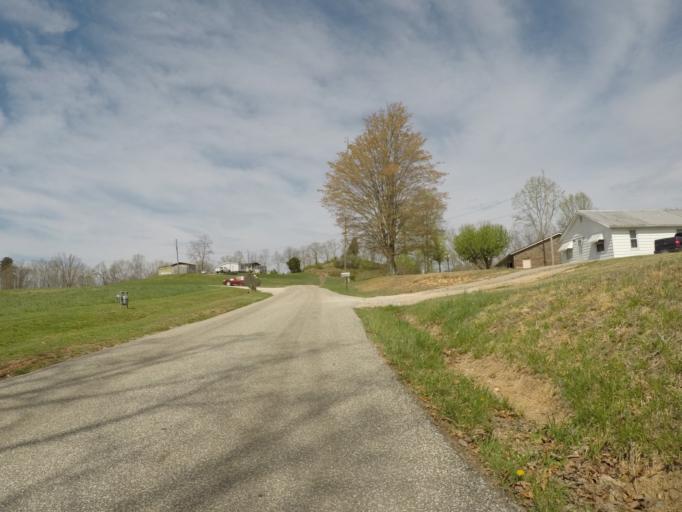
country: US
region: West Virginia
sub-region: Wayne County
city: Lavalette
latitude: 38.3312
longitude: -82.3625
